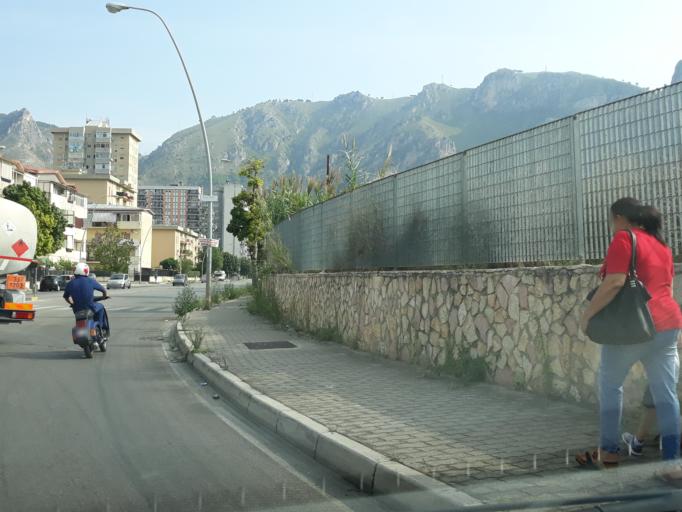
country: IT
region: Sicily
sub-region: Palermo
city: Villa Ciambra
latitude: 38.0848
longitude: 13.3556
